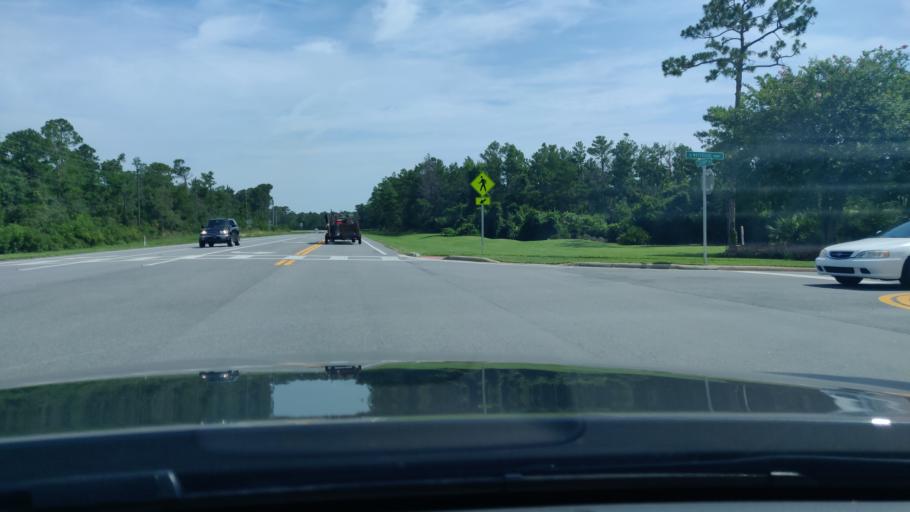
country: US
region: Florida
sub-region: Flagler County
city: Flagler Beach
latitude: 29.5271
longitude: -81.1703
